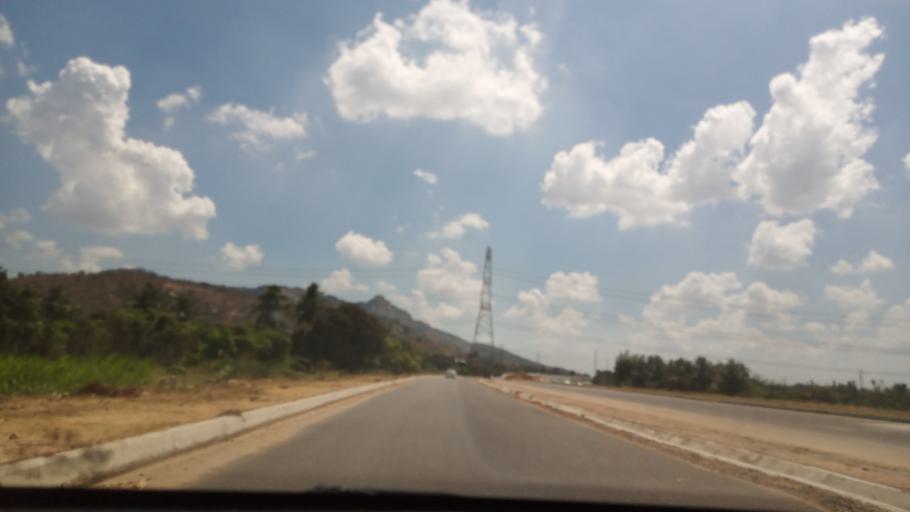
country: IN
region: Andhra Pradesh
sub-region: Chittoor
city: Pakala
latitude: 13.3420
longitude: 79.0817
